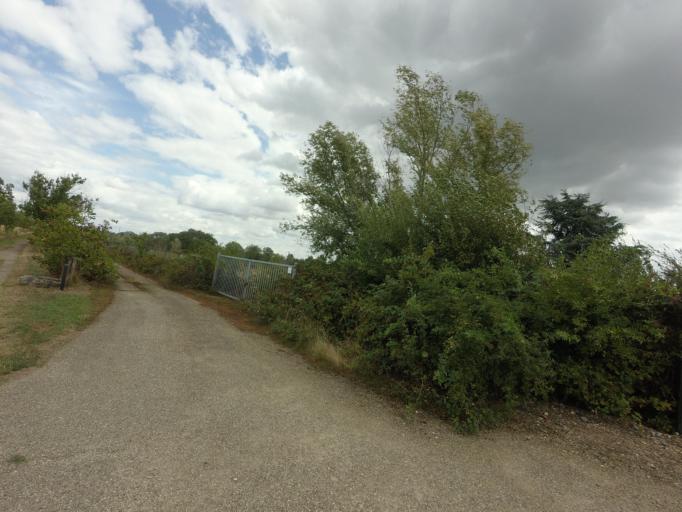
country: NL
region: Limburg
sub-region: Gemeente Maasgouw
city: Maasbracht
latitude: 51.1315
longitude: 5.8622
